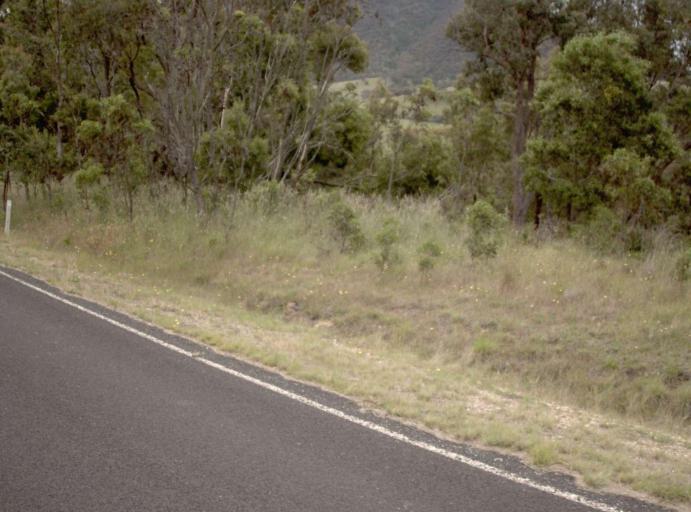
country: AU
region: Victoria
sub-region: East Gippsland
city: Bairnsdale
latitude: -37.5660
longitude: 147.1880
